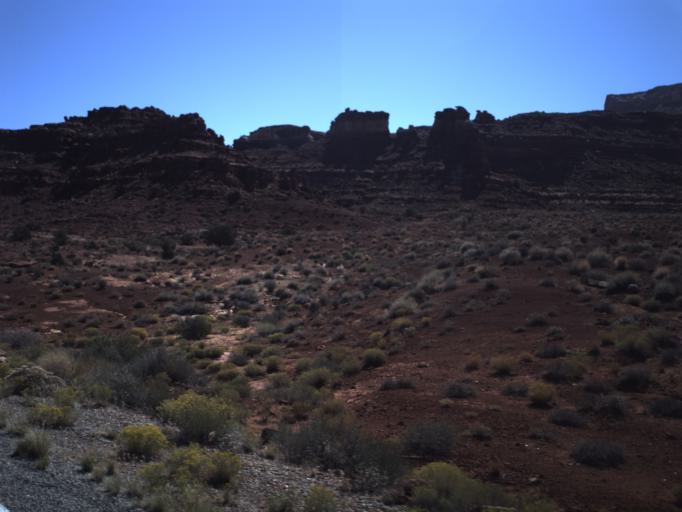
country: US
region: Utah
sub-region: San Juan County
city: Blanding
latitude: 37.8106
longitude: -110.3364
